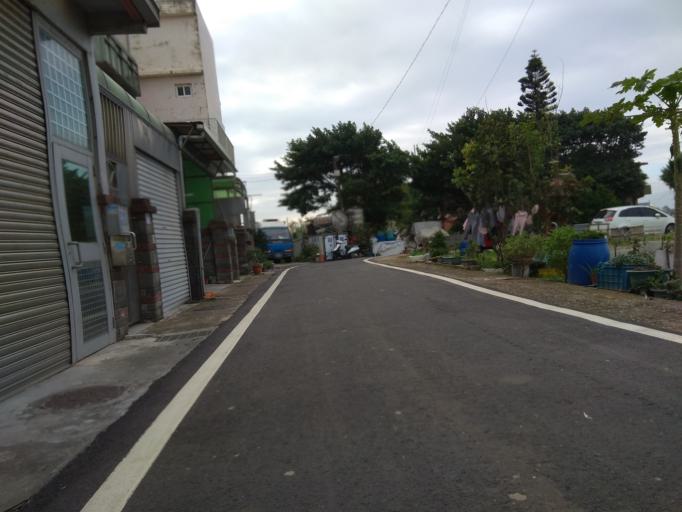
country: TW
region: Taiwan
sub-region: Hsinchu
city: Zhubei
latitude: 24.9827
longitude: 121.0537
